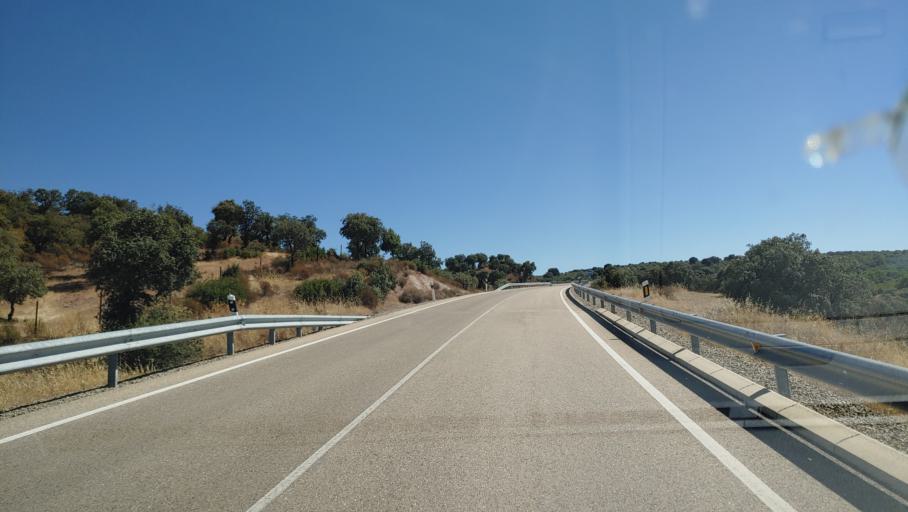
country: ES
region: Andalusia
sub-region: Provincia de Jaen
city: Genave
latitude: 38.4860
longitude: -2.7668
